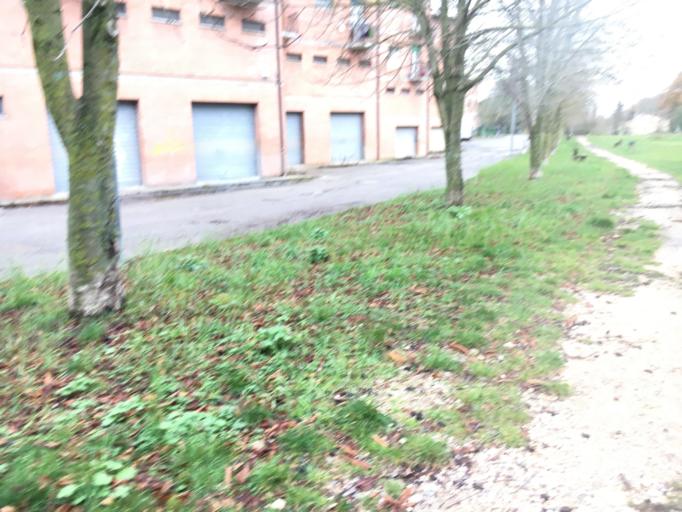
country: IT
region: Umbria
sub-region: Provincia di Perugia
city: Perugia
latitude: 43.1188
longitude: 12.3726
